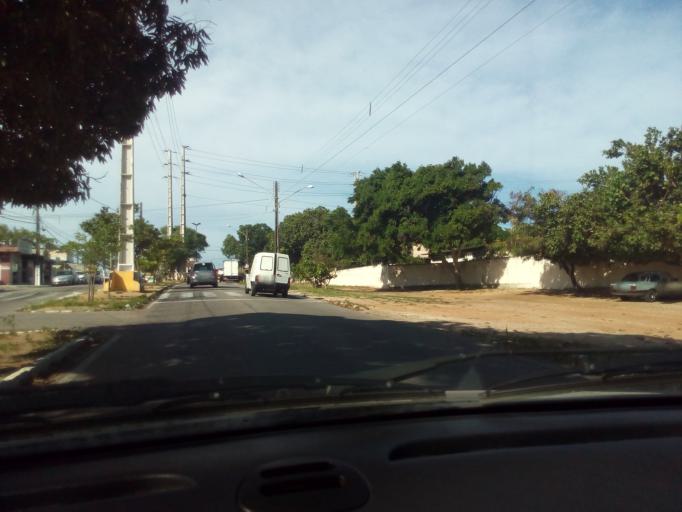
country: BR
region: Rio Grande do Norte
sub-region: Natal
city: Natal
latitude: -5.8663
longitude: -35.2072
